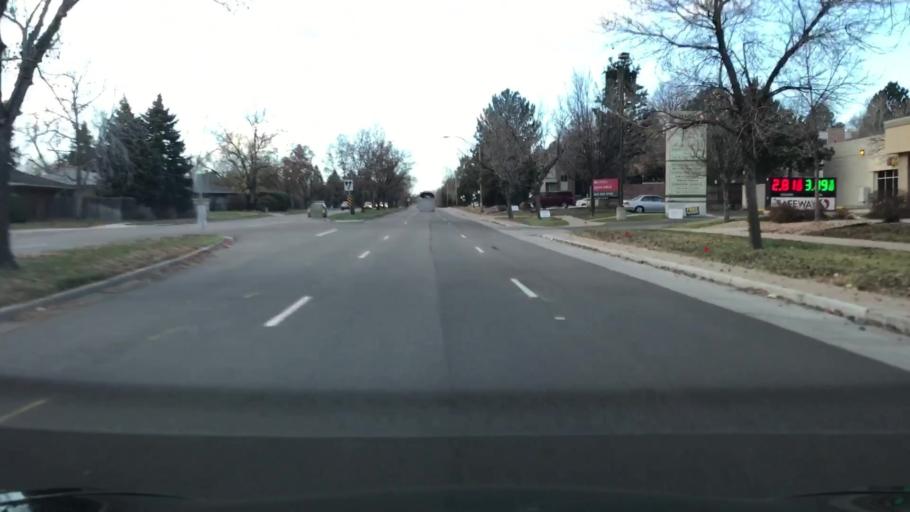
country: US
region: Colorado
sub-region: Arapahoe County
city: Glendale
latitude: 39.6667
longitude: -104.9131
